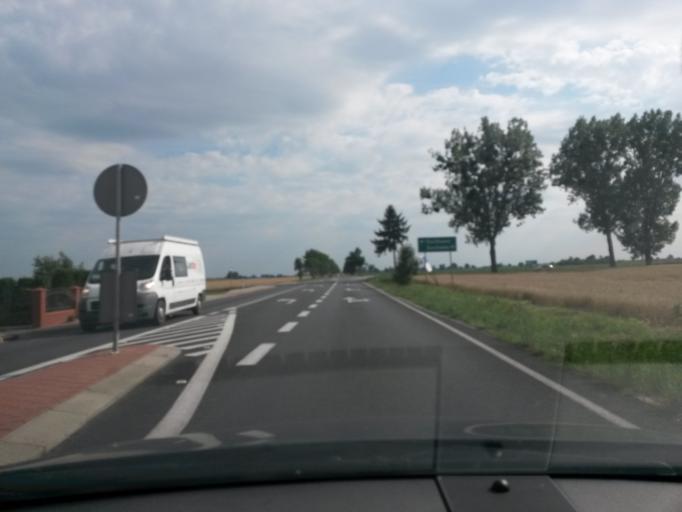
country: PL
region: Greater Poland Voivodeship
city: Miejska Gorka
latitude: 51.7012
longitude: 16.9468
